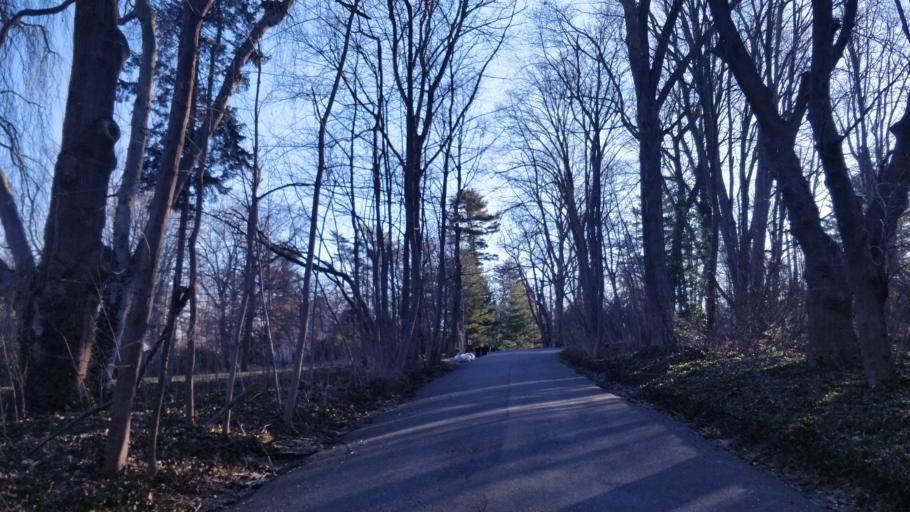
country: US
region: New York
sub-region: Nassau County
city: Glen Cove
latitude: 40.8779
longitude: -73.6501
